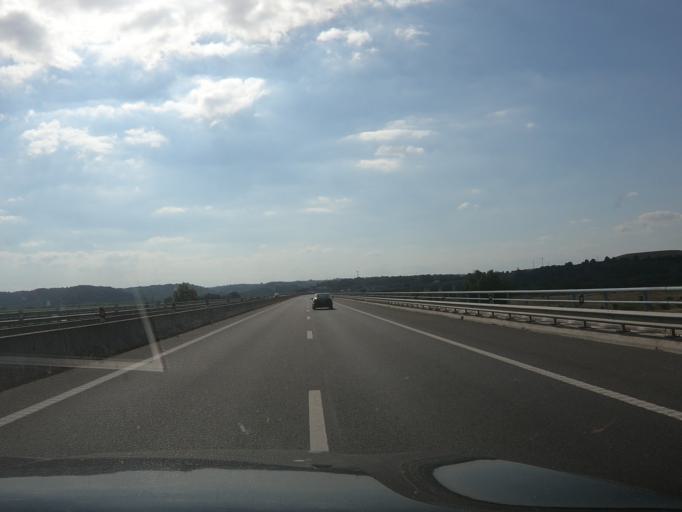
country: PT
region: Santarem
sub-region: Santarem
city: Santarem
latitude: 39.2031
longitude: -8.6893
